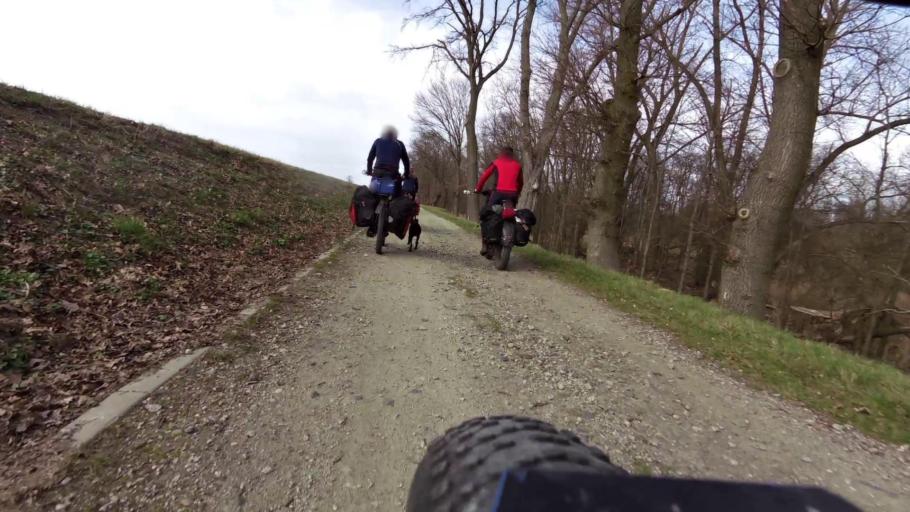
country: DE
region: Brandenburg
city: Reitwein
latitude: 52.5195
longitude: 14.6120
